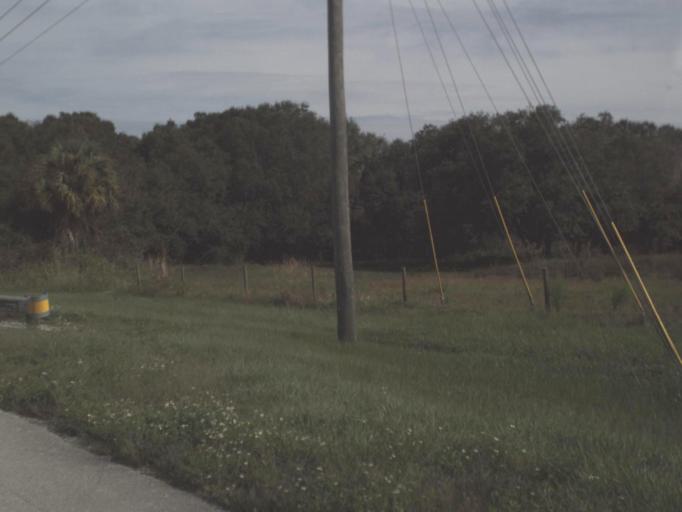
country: US
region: Florida
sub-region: DeSoto County
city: Nocatee
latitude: 27.0498
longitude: -81.7830
